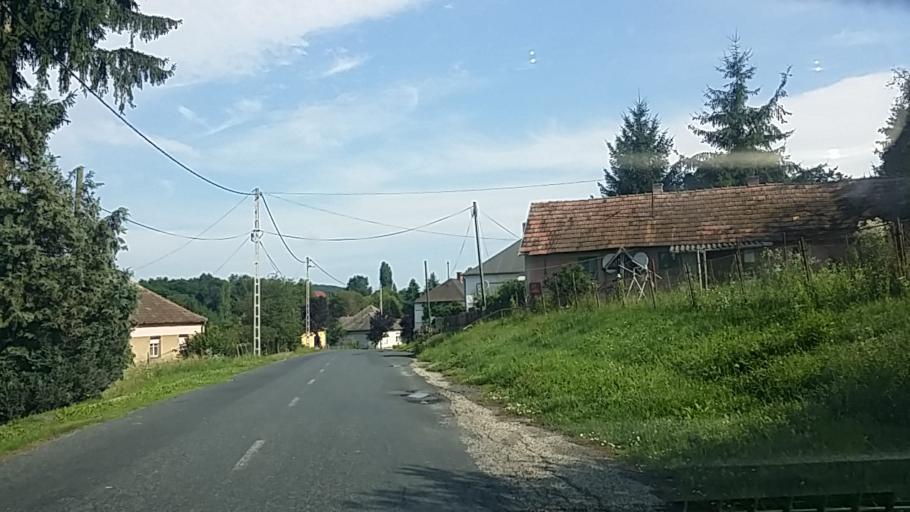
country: HU
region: Zala
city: Letenye
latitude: 46.5338
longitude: 16.7038
